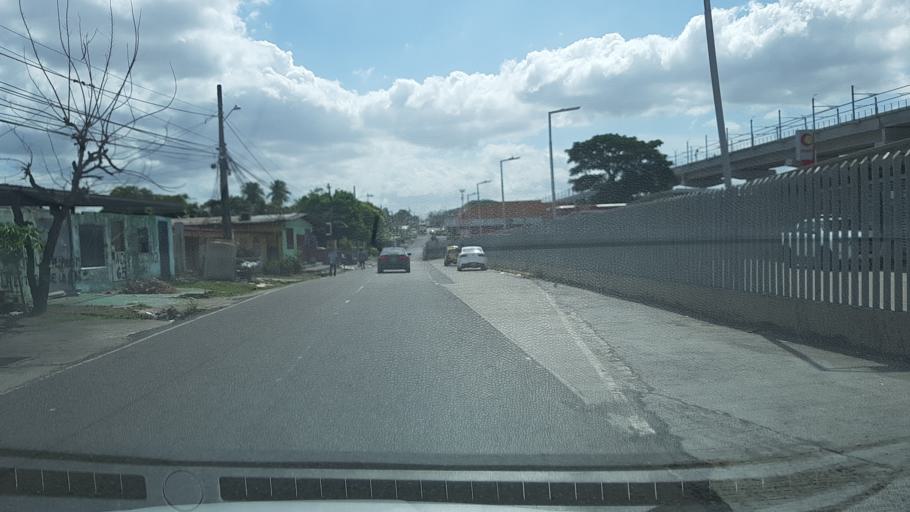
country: PA
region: Panama
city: San Miguelito
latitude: 9.0604
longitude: -79.4296
